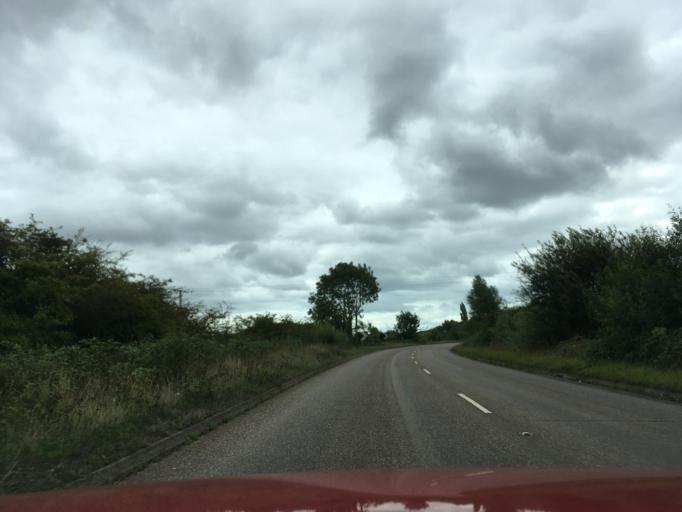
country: GB
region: England
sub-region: Devon
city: Exminster
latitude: 50.6784
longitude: -3.4863
